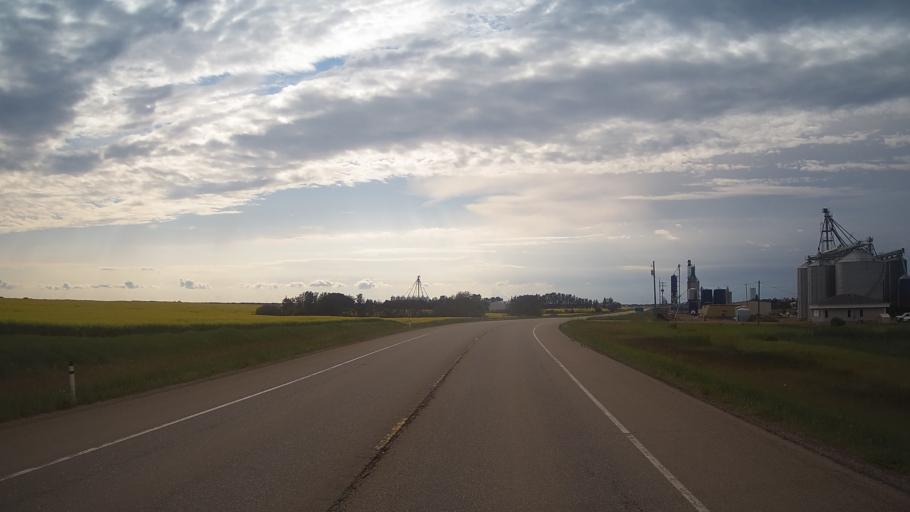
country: CA
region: Alberta
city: Viking
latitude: 53.0879
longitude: -111.7654
